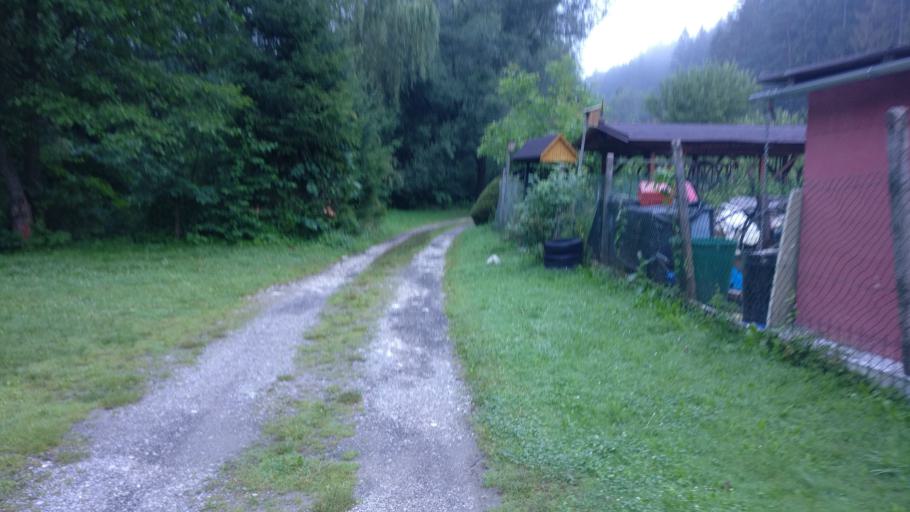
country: SK
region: Zilinsky
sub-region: Okres Zilina
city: Zilina
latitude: 49.2434
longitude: 18.7554
